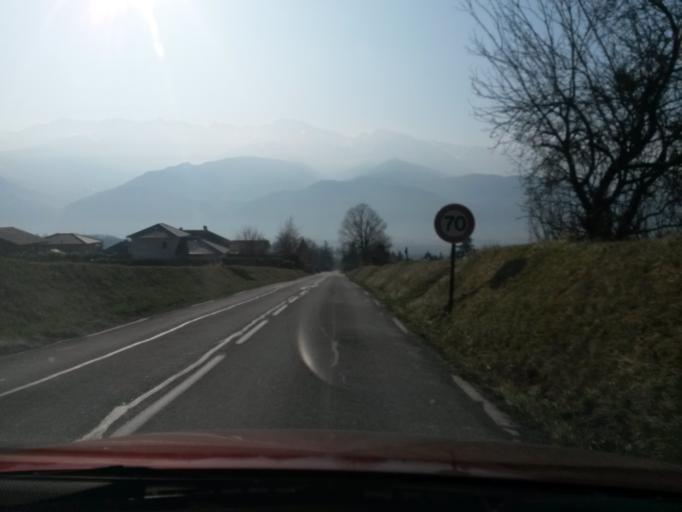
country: FR
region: Rhone-Alpes
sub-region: Departement de l'Isere
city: Saint-Nazaire-les-Eymes
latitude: 45.2639
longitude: 5.8412
